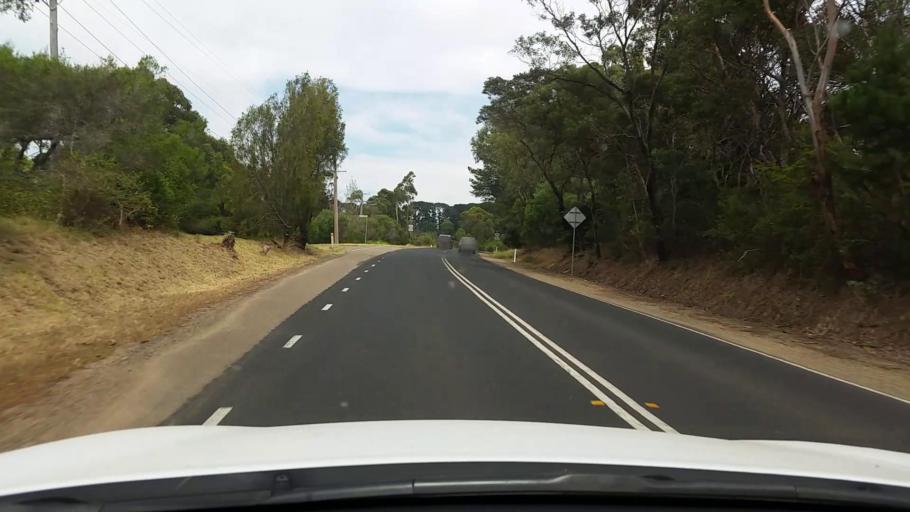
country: AU
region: Victoria
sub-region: Mornington Peninsula
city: Merricks
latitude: -38.4167
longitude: 145.0495
